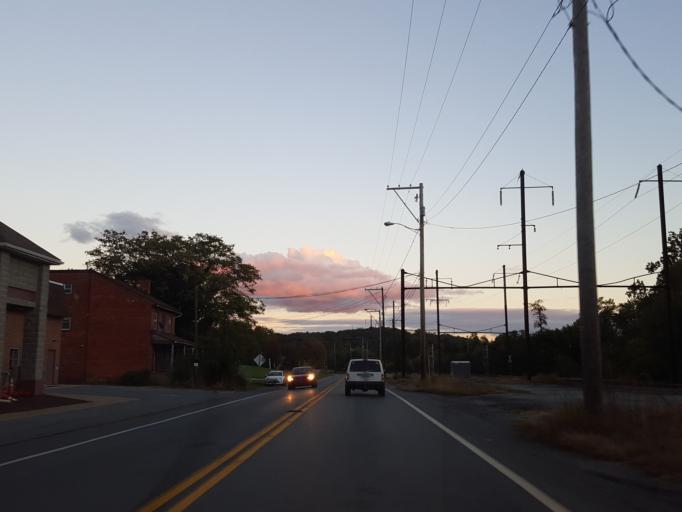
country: US
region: Pennsylvania
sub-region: Lancaster County
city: Columbia
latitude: 40.0285
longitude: -76.5035
